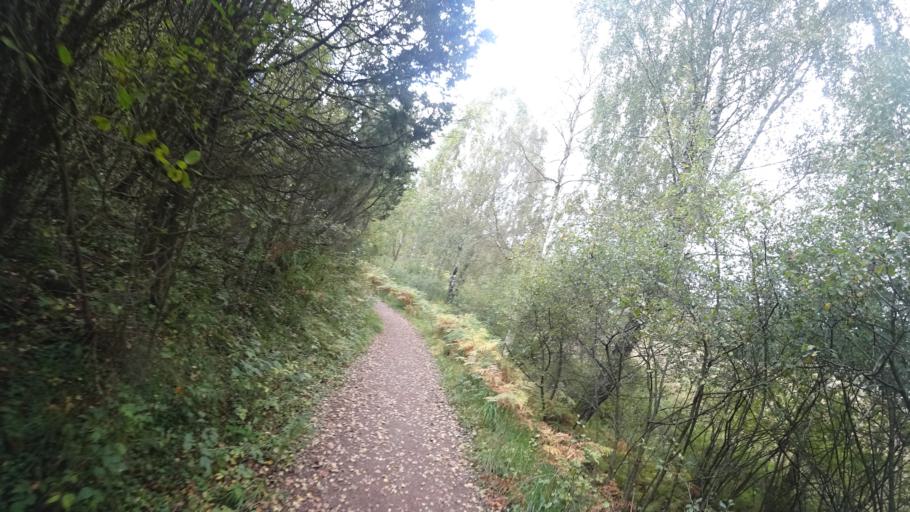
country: SE
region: Vaestra Goetaland
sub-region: Goteborg
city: Billdal
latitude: 57.6091
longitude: 11.9695
